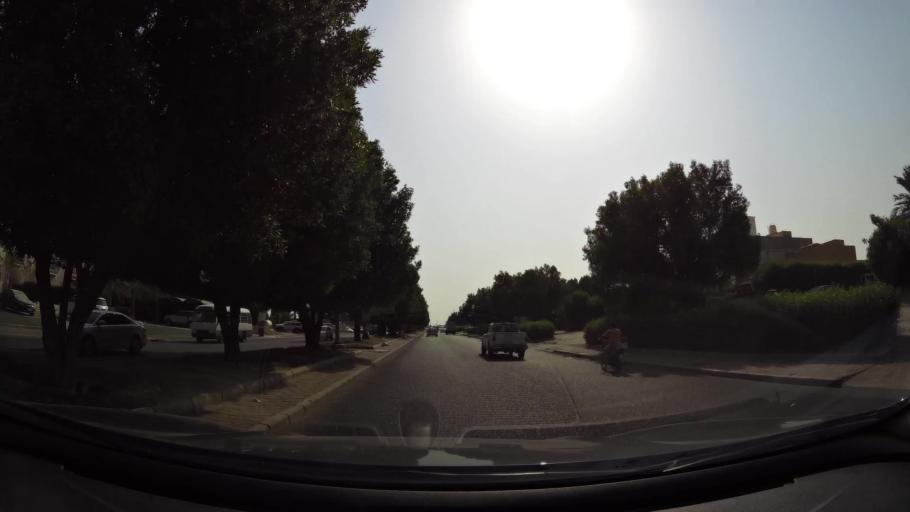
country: KW
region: Muhafazat al Jahra'
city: Al Jahra'
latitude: 29.3230
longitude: 47.6606
